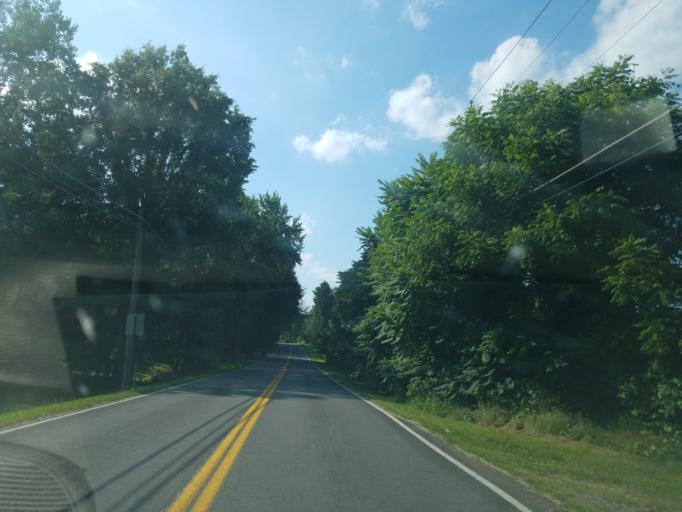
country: US
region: Ohio
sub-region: Summit County
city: Mogadore
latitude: 41.0484
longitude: -81.3661
